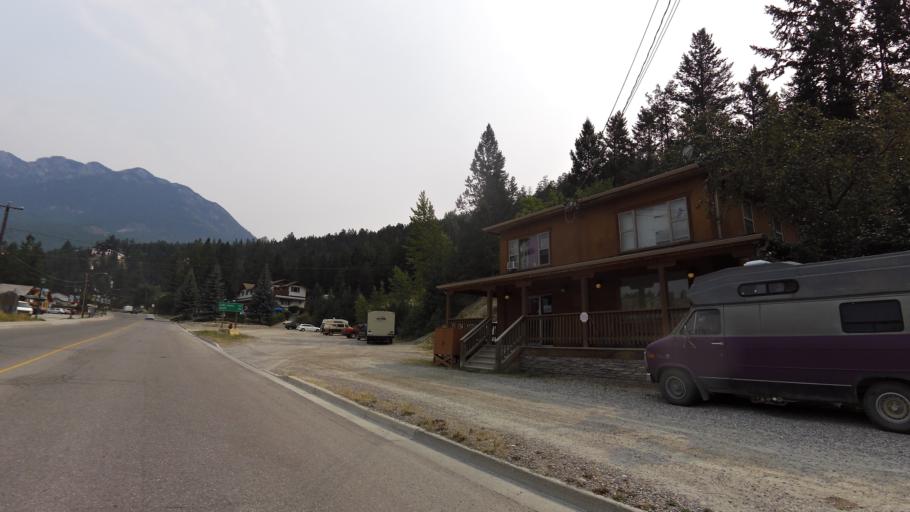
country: CA
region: British Columbia
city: Invermere
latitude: 50.6242
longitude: -116.0691
